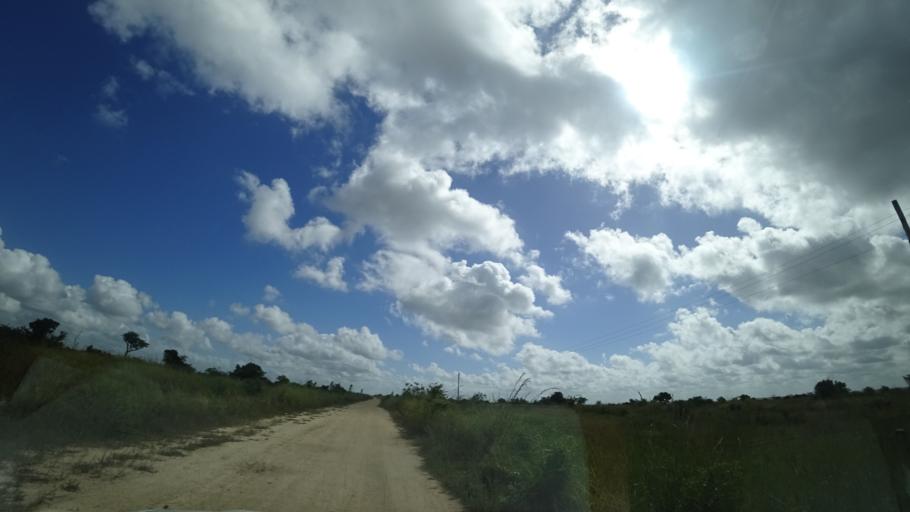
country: MZ
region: Sofala
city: Dondo
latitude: -19.4320
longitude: 34.5609
